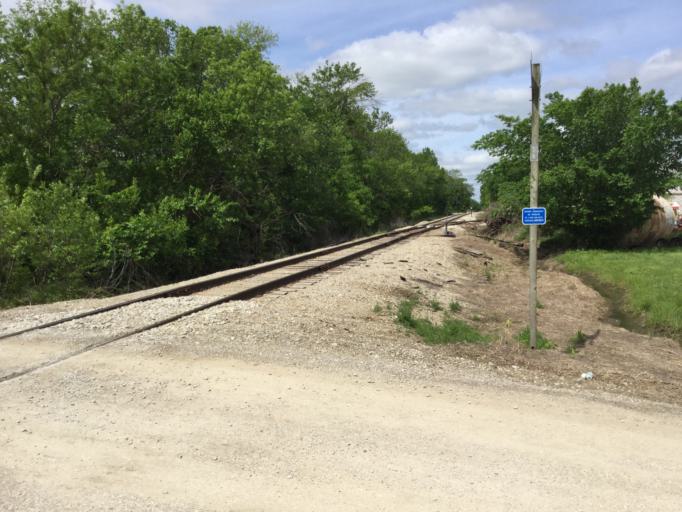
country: US
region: Kansas
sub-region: Labette County
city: Altamont
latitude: 37.2075
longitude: -95.4013
